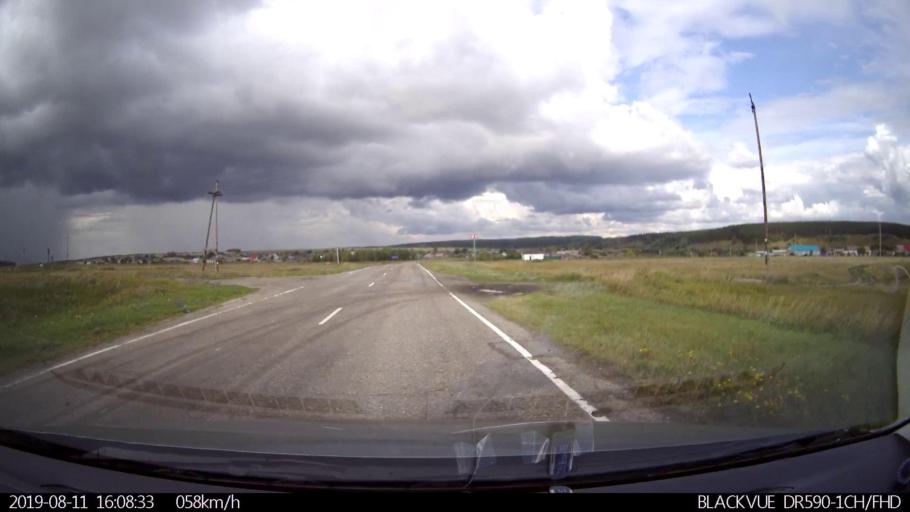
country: RU
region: Ulyanovsk
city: Ignatovka
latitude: 53.9856
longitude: 47.6484
